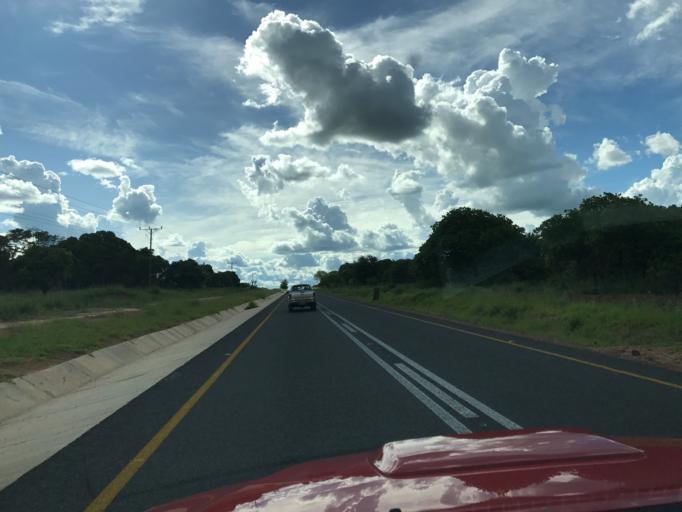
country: MZ
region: Nampula
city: Nampula
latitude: -15.0049
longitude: 38.9852
